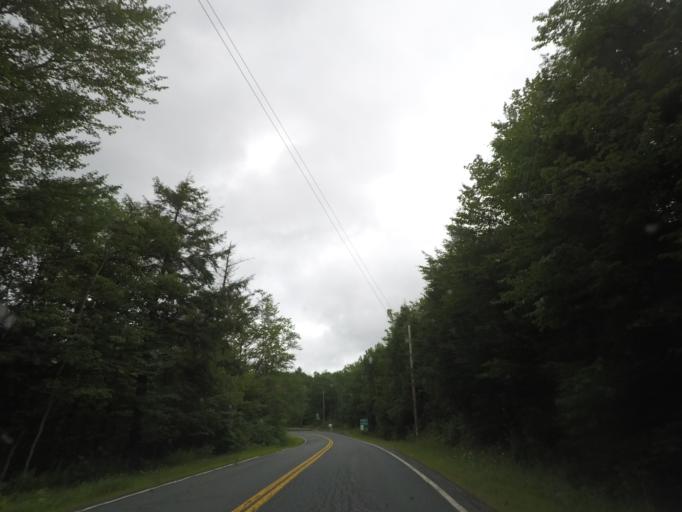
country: US
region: New York
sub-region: Rensselaer County
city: Poestenkill
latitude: 42.6892
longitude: -73.4443
